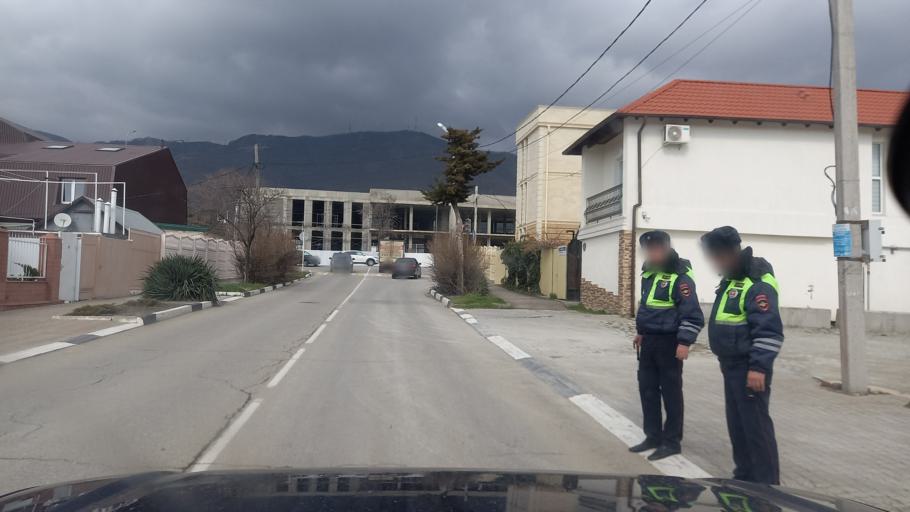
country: RU
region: Krasnodarskiy
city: Gelendzhik
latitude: 44.5605
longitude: 38.0923
